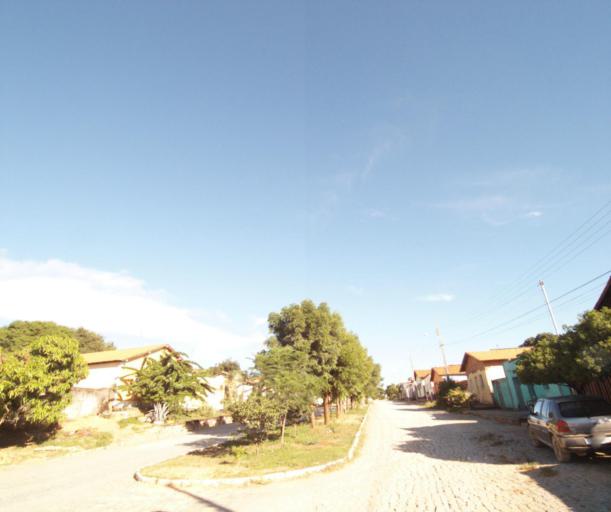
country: BR
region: Minas Gerais
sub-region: Manga
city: Manga
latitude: -14.3138
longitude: -44.4609
